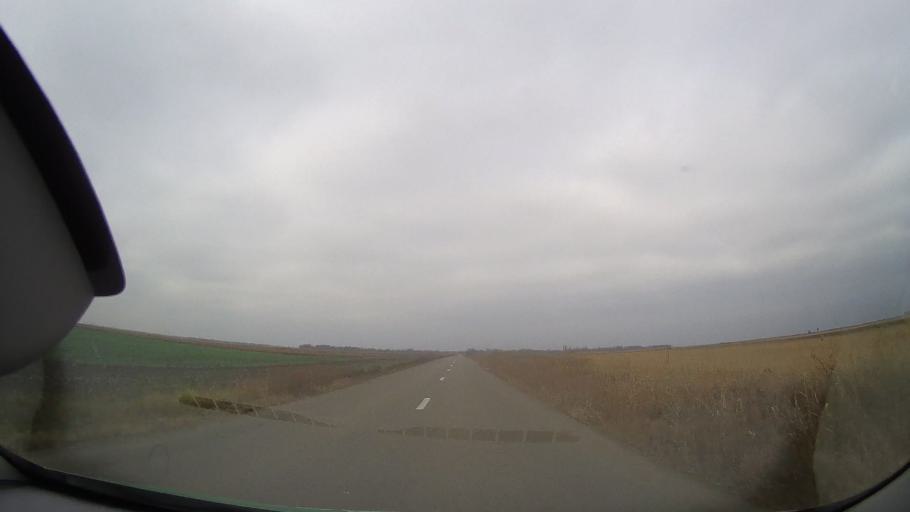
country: RO
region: Buzau
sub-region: Comuna Scutelnici
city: Scutelnici
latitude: 44.8646
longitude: 26.8957
